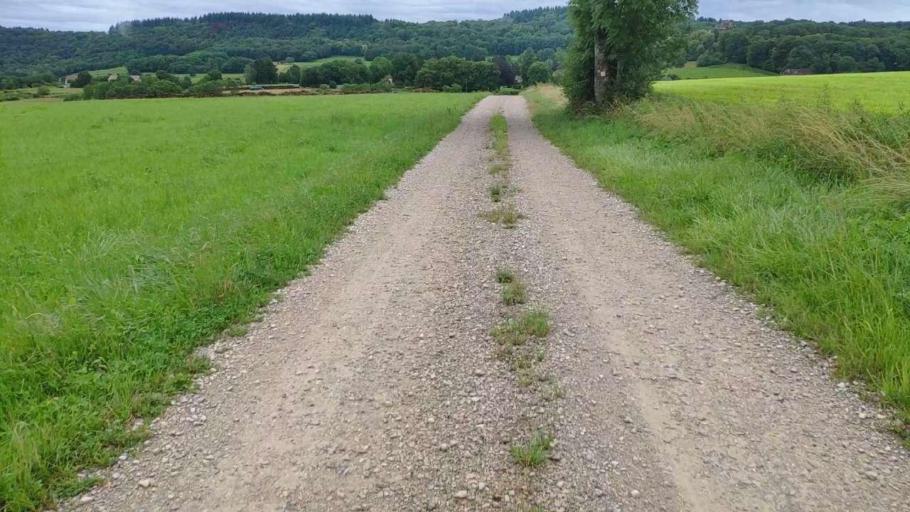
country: FR
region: Franche-Comte
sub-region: Departement du Jura
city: Poligny
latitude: 46.7881
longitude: 5.6064
